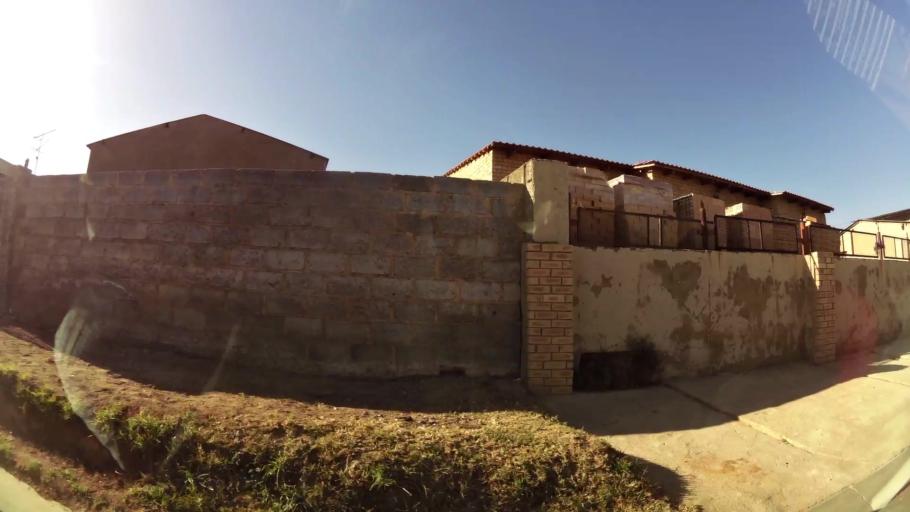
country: ZA
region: Gauteng
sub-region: Ekurhuleni Metropolitan Municipality
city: Tembisa
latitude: -26.0309
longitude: 28.2125
